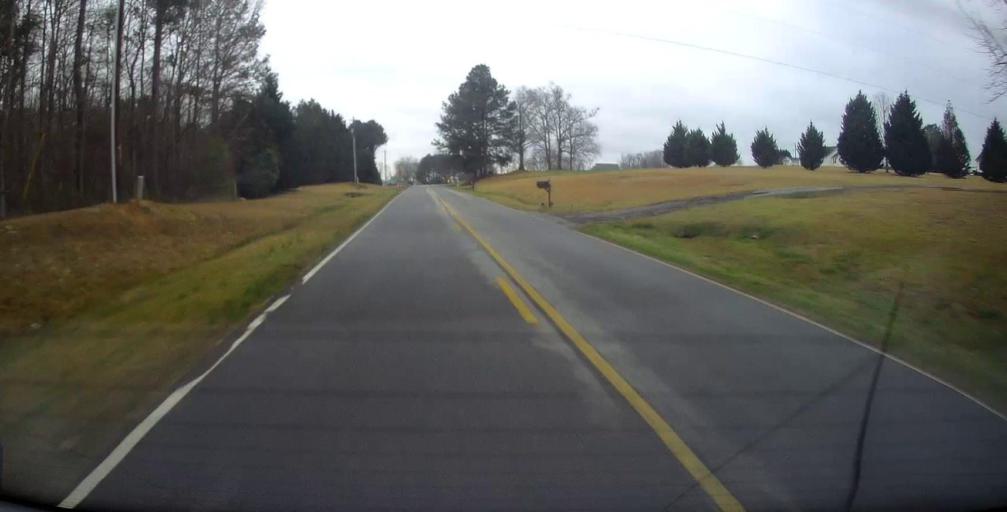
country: US
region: Georgia
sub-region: Pike County
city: Zebulon
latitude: 33.0524
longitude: -84.3235
